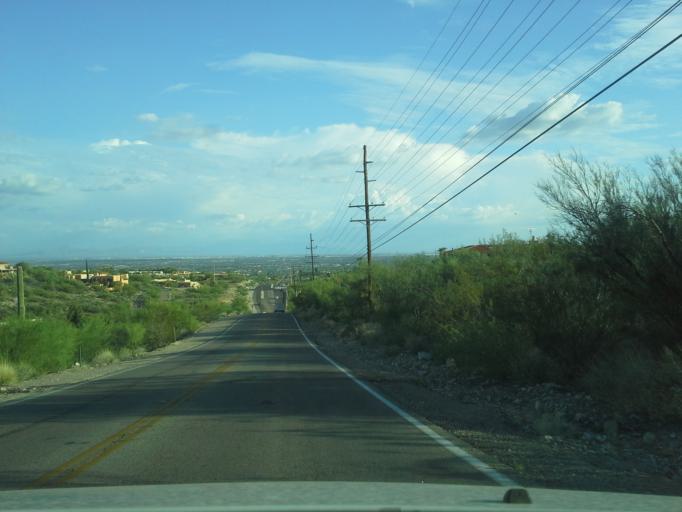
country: US
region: Arizona
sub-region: Pima County
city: Catalina Foothills
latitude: 32.3137
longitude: -110.8752
